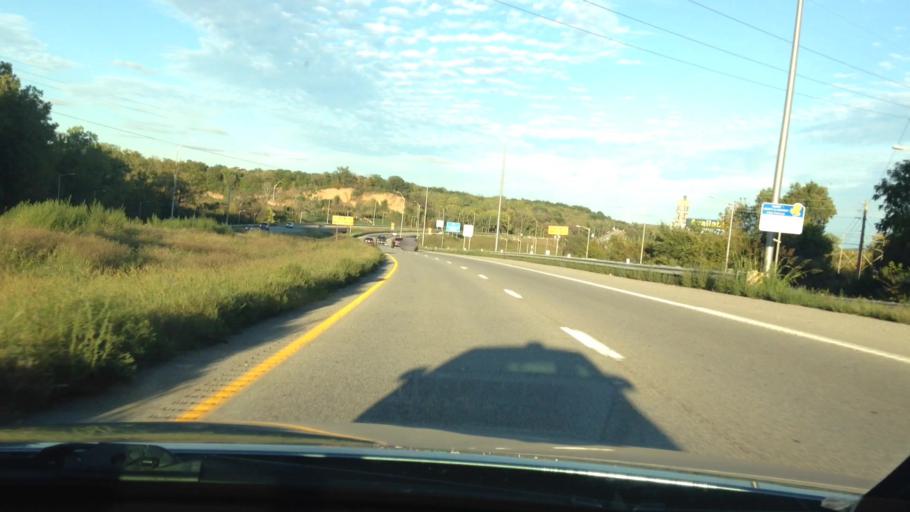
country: US
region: Missouri
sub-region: Clay County
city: North Kansas City
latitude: 39.1519
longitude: -94.5250
